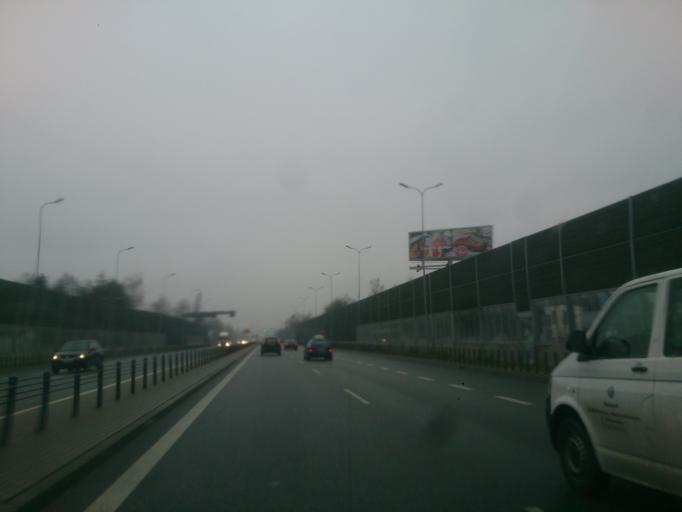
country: PL
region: Masovian Voivodeship
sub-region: Powiat warszawski zachodni
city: Lomianki
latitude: 52.3296
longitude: 20.8978
